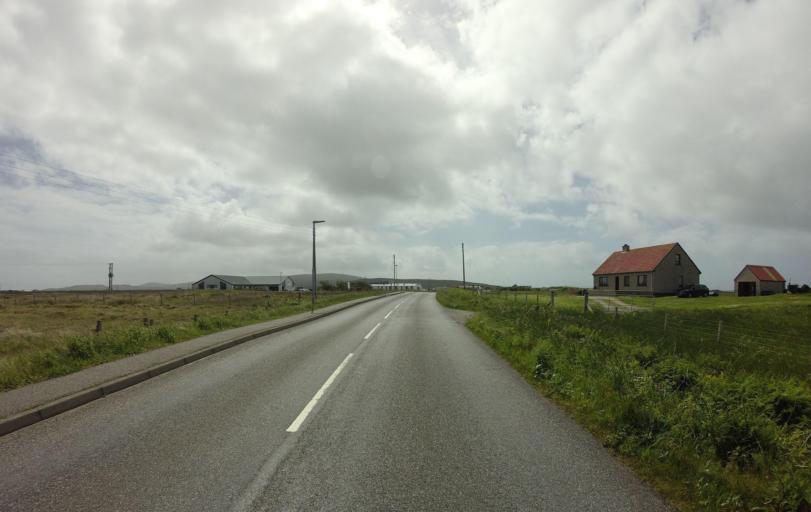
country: GB
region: Scotland
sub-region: Eilean Siar
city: Isle of South Uist
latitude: 57.1636
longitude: -7.3695
